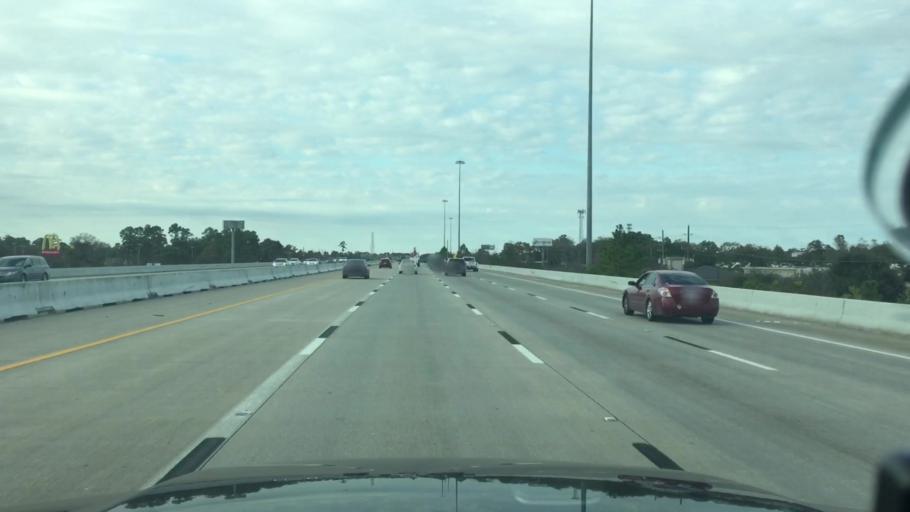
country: US
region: Texas
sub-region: Harris County
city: Oak Cliff Place
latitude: 29.9985
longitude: -95.5806
